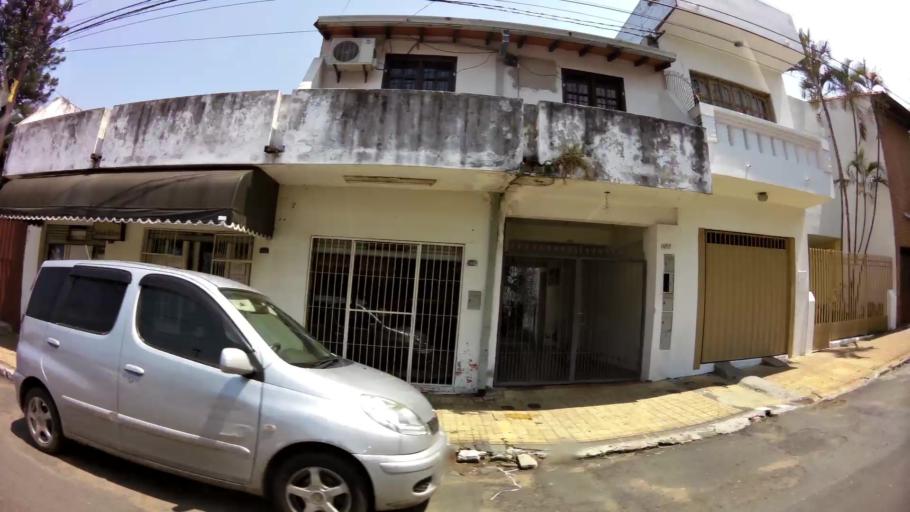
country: PY
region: Asuncion
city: Asuncion
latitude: -25.2935
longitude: -57.6429
